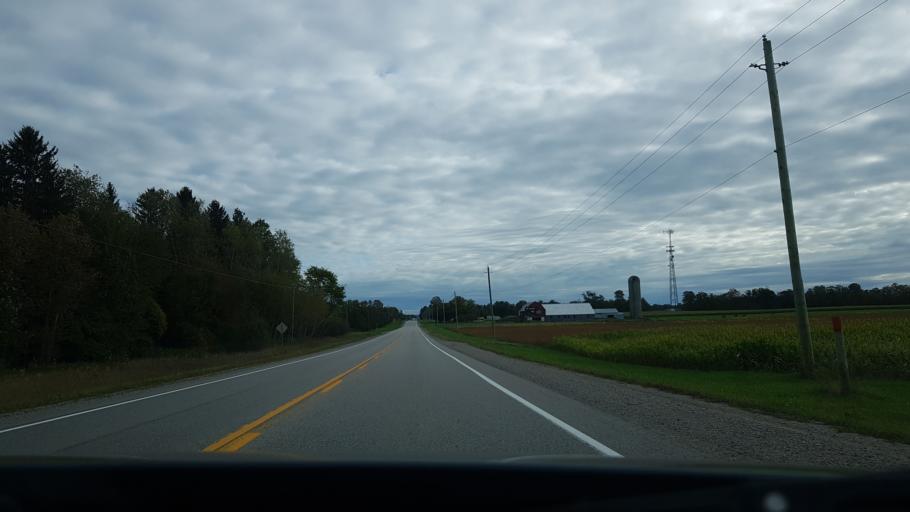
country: CA
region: Ontario
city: Barrie
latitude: 44.4944
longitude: -79.8033
